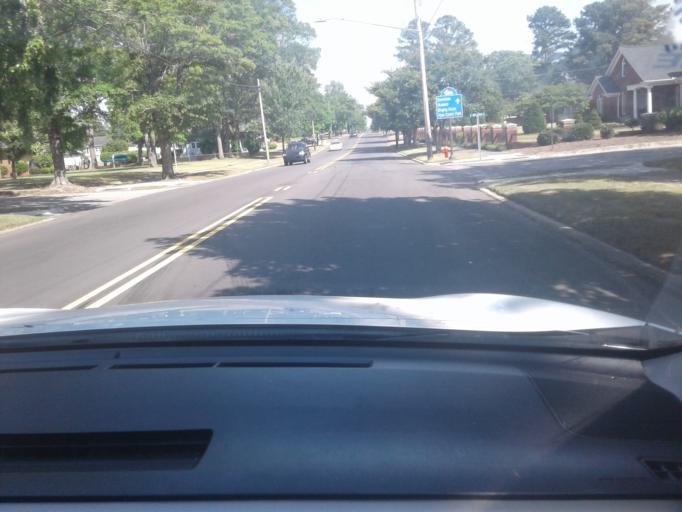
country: US
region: North Carolina
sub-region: Johnston County
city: Benson
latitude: 35.3858
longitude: -78.5556
